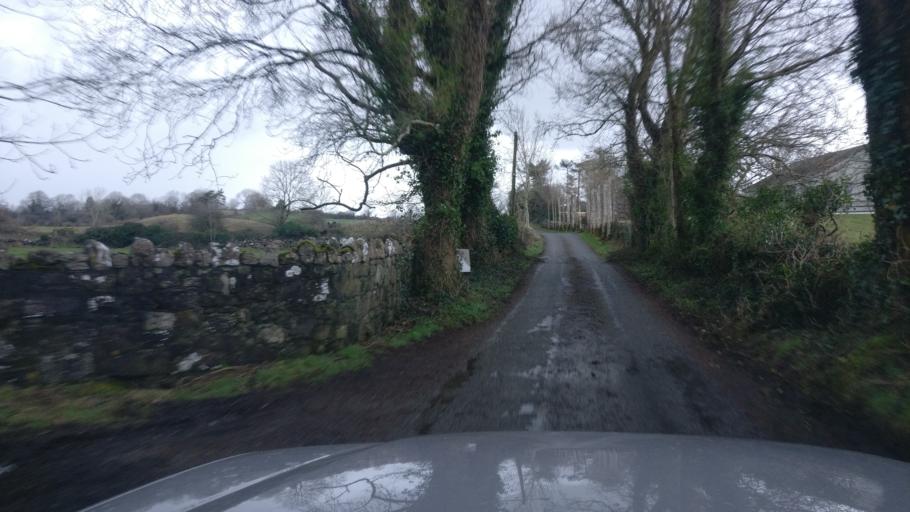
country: IE
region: Connaught
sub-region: County Galway
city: Loughrea
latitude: 53.1861
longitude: -8.6642
